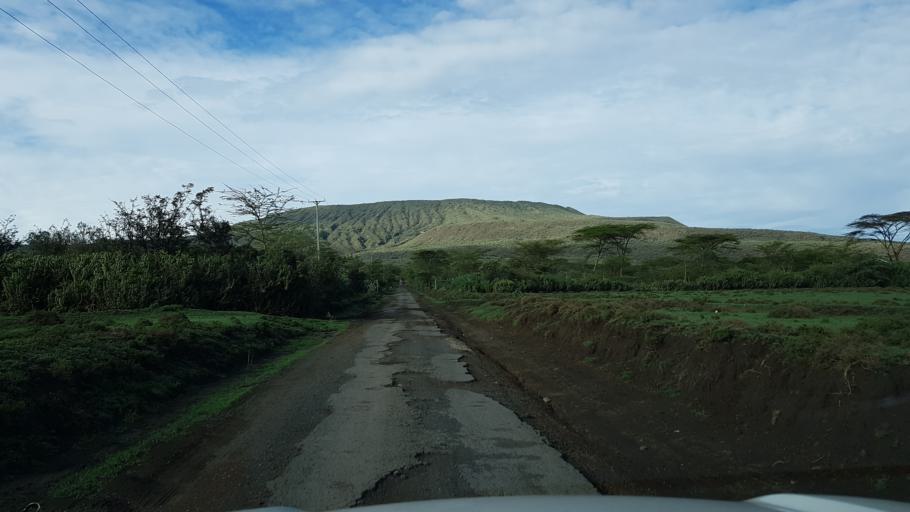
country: KE
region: Nakuru
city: Kijabe
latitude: -0.8856
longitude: 36.4769
